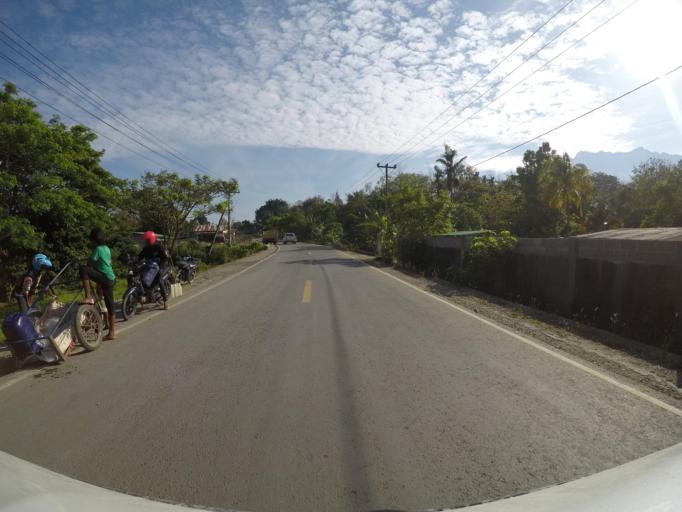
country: TL
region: Bobonaro
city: Maliana
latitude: -8.9863
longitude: 125.2219
